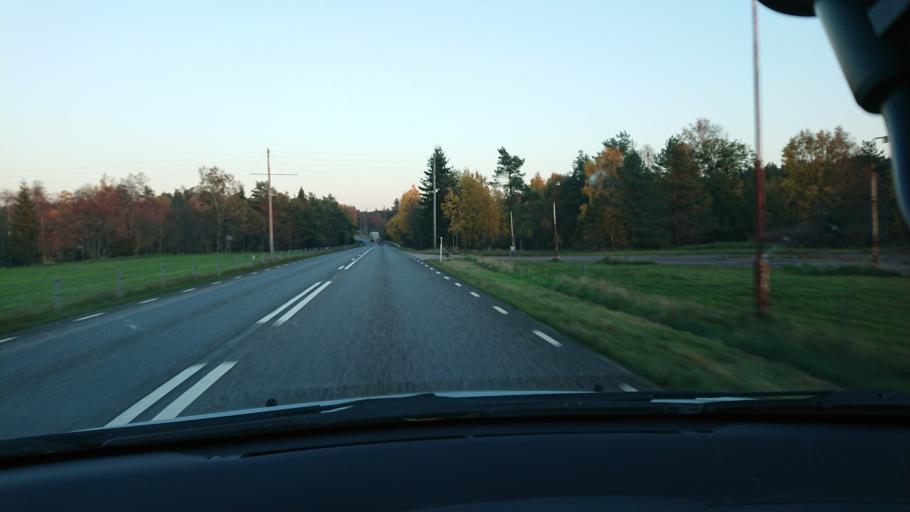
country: SE
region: Halland
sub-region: Laholms Kommun
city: Knared
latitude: 56.7131
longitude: 13.2522
